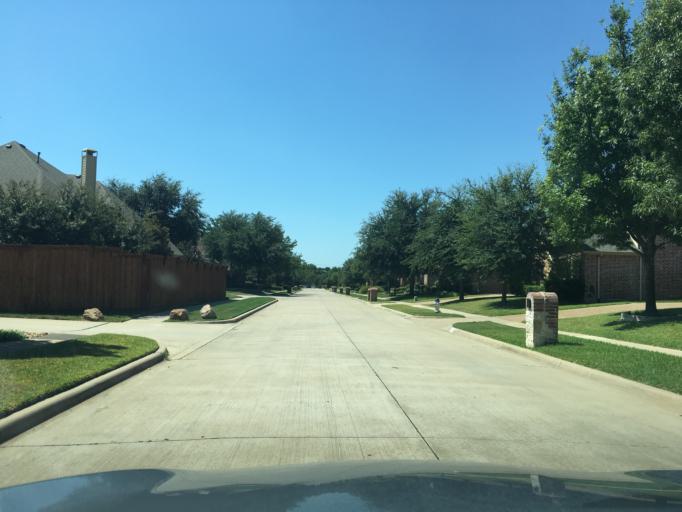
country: US
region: Texas
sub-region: Dallas County
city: Sachse
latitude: 32.9680
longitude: -96.6161
